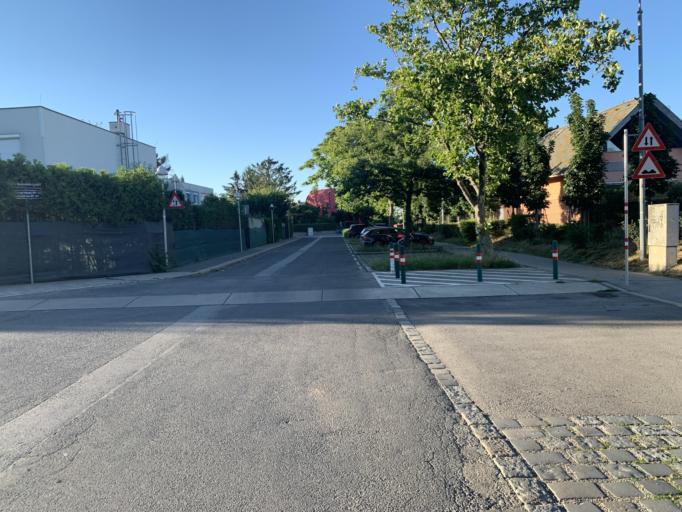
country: AT
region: Lower Austria
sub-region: Politischer Bezirk Wien-Umgebung
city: Leopoldsdorf
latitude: 48.1525
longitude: 16.4069
